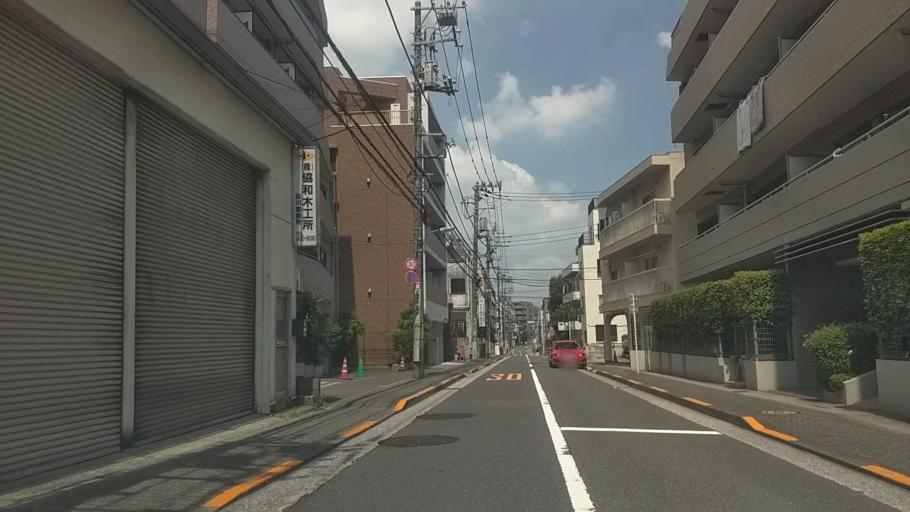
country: JP
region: Tokyo
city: Tokyo
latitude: 35.6223
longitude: 139.7126
